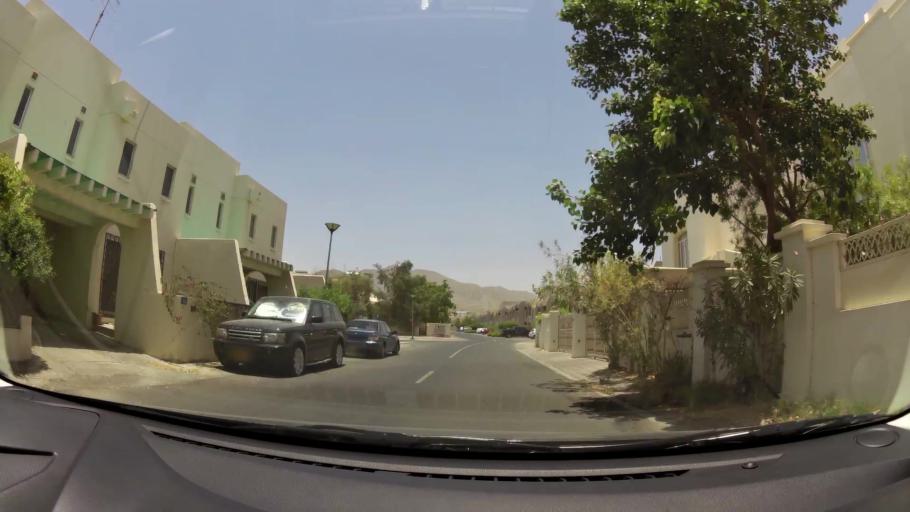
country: OM
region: Muhafazat Masqat
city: Bawshar
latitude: 23.5964
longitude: 58.4590
